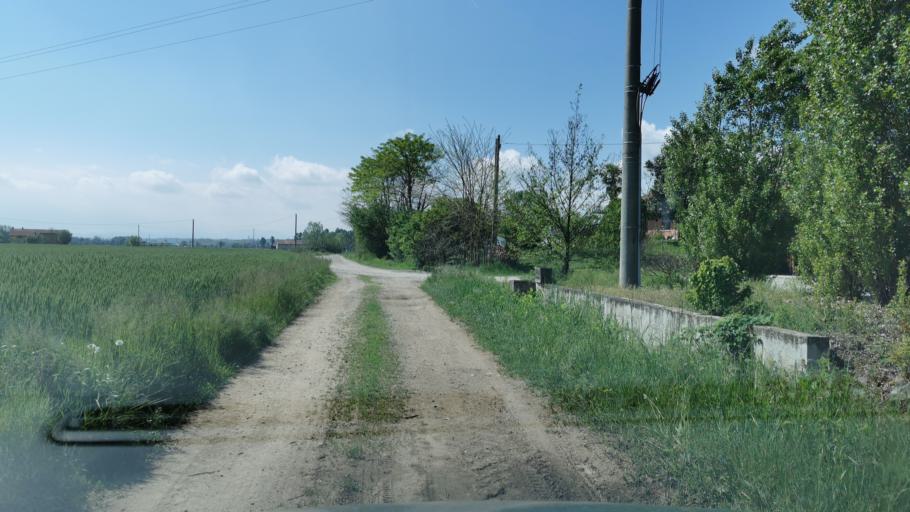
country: IT
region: Piedmont
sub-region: Provincia di Torino
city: Feletto
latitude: 45.2818
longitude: 7.7224
